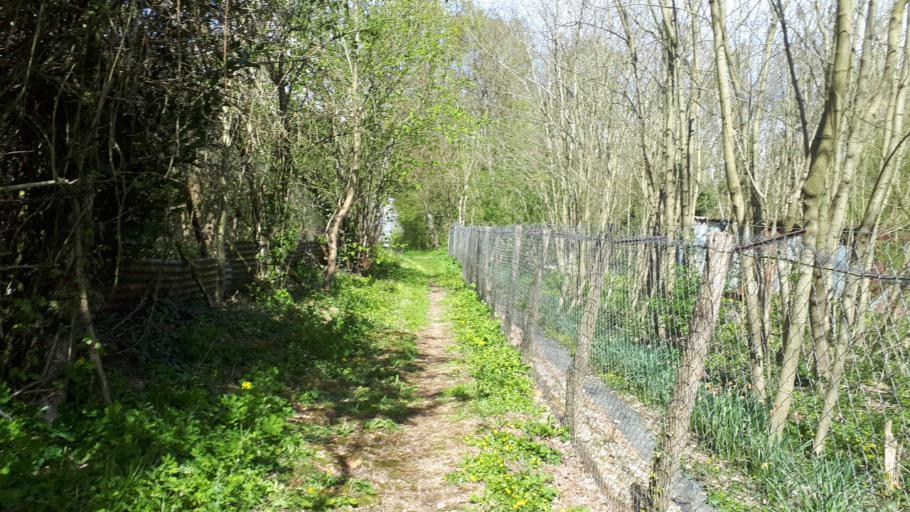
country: FR
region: Centre
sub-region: Departement du Loir-et-Cher
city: Villiers-sur-Loir
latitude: 47.7884
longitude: 0.9682
